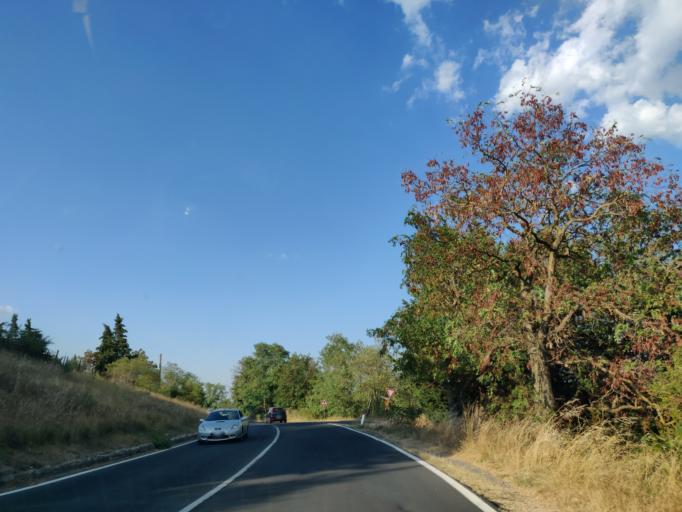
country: IT
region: Tuscany
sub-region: Provincia di Siena
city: Abbadia San Salvatore
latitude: 42.8694
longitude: 11.6838
